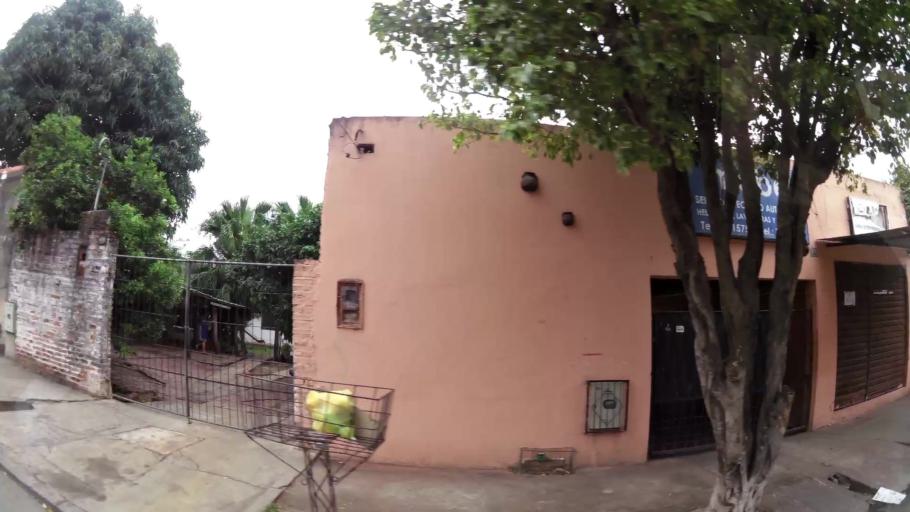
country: BO
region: Santa Cruz
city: Santa Cruz de la Sierra
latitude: -17.7590
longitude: -63.1591
